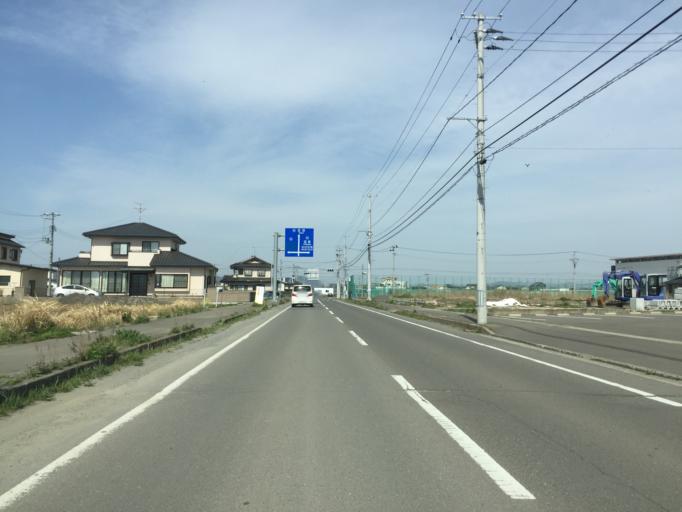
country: JP
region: Miyagi
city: Watari
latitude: 38.0414
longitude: 140.9107
